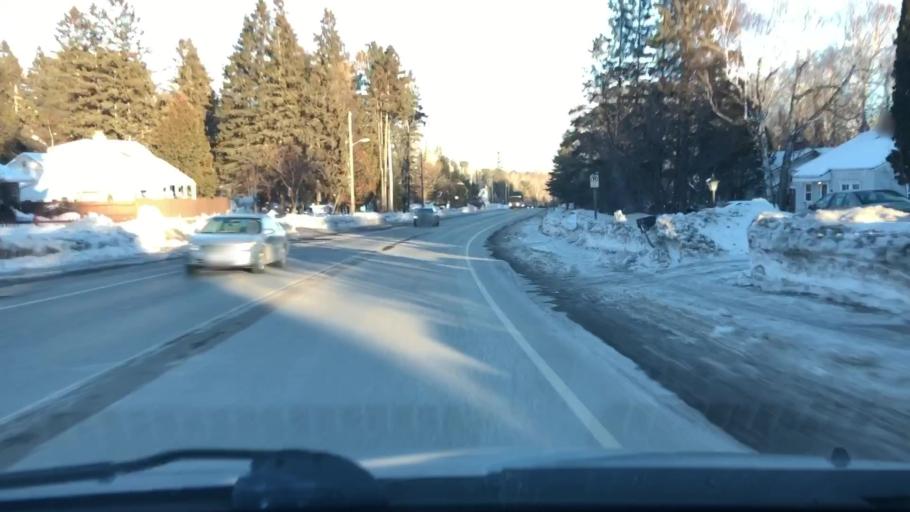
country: US
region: Minnesota
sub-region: Saint Louis County
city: Duluth
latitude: 46.8251
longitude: -92.0907
